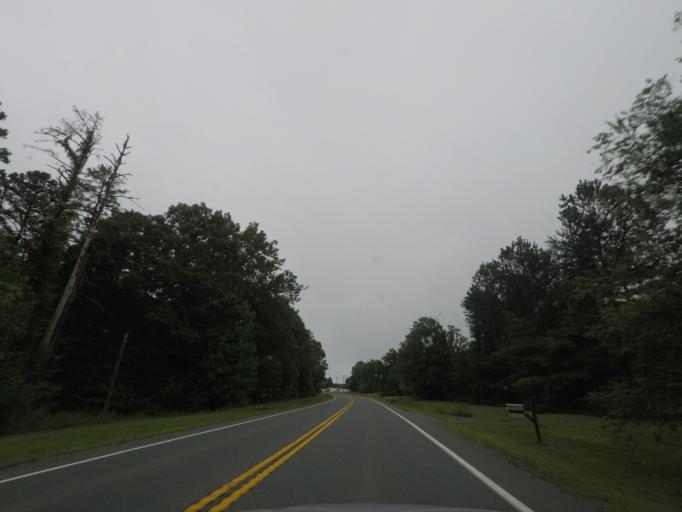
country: US
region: Virginia
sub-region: Fluvanna County
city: Weber City
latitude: 37.7444
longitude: -78.2891
